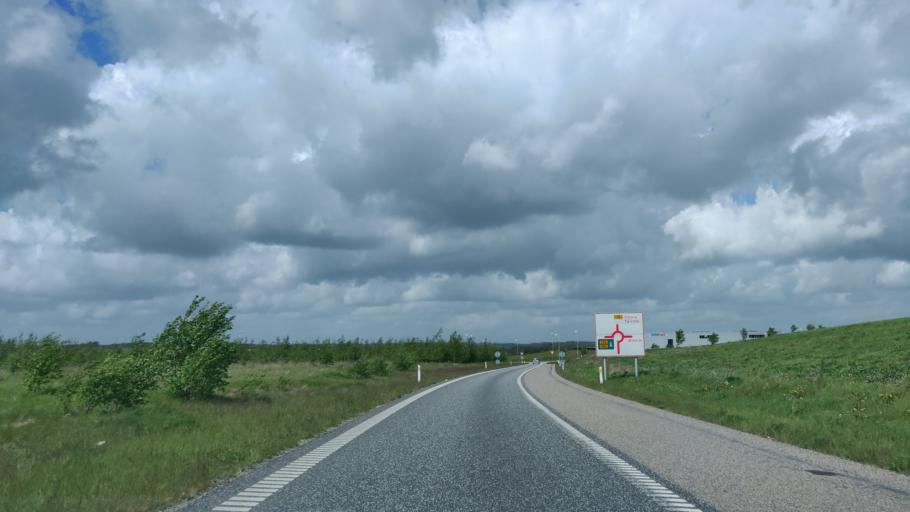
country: DK
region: Central Jutland
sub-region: Hedensted Kommune
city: Torring
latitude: 55.8307
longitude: 9.5193
